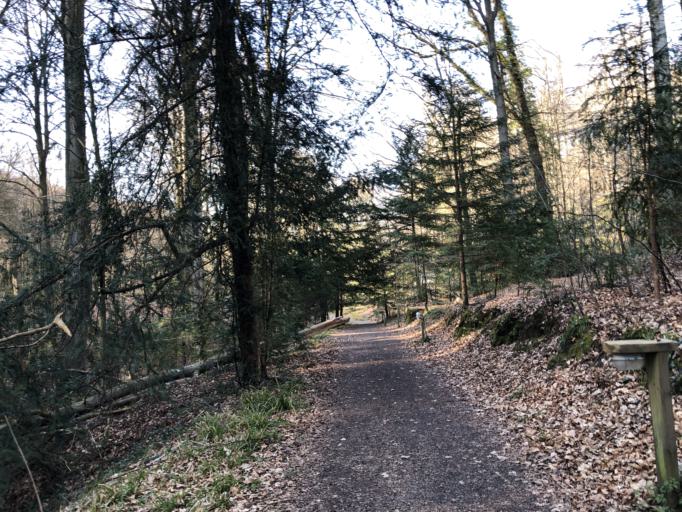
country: DK
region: South Denmark
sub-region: Vejle Kommune
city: Borkop
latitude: 55.6892
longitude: 9.6163
